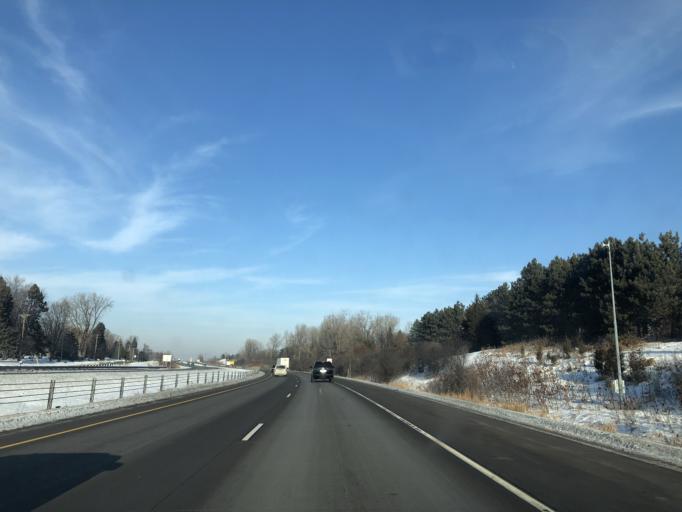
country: US
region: Minnesota
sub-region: Ramsey County
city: Shoreview
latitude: 45.0732
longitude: -93.1695
